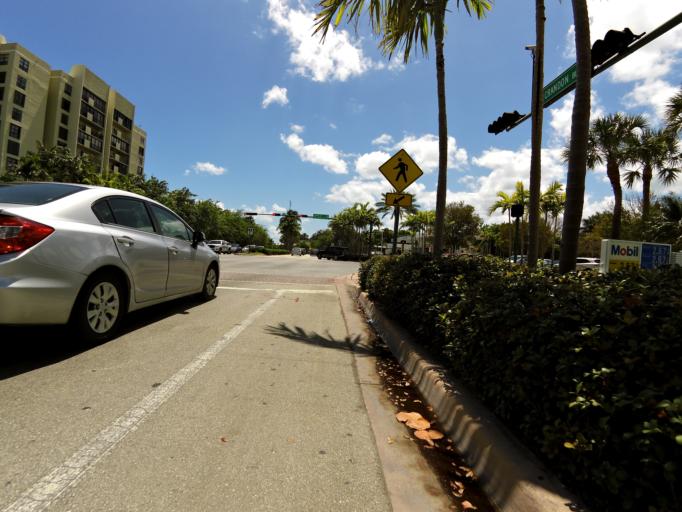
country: US
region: Florida
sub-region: Miami-Dade County
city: Lakes by the Bay
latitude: 25.4862
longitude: -80.2670
